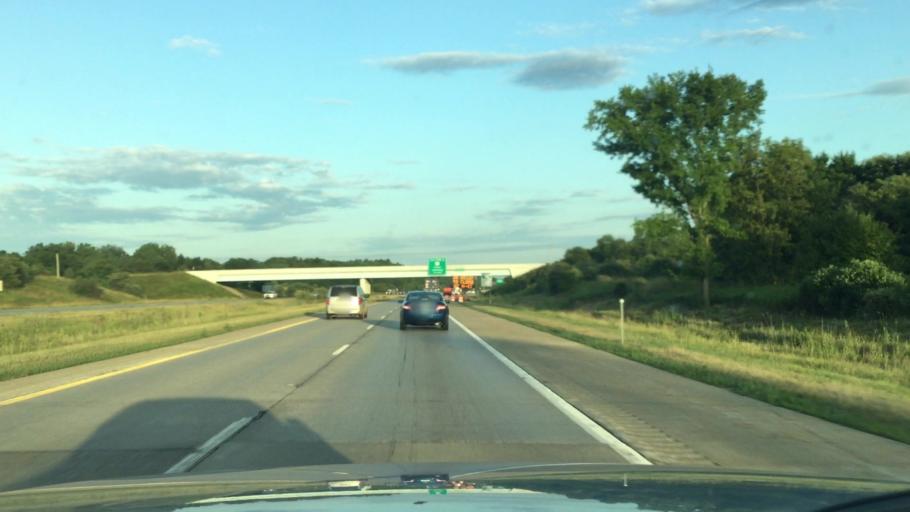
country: US
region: Michigan
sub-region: Clinton County
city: Bath
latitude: 42.8031
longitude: -84.4806
